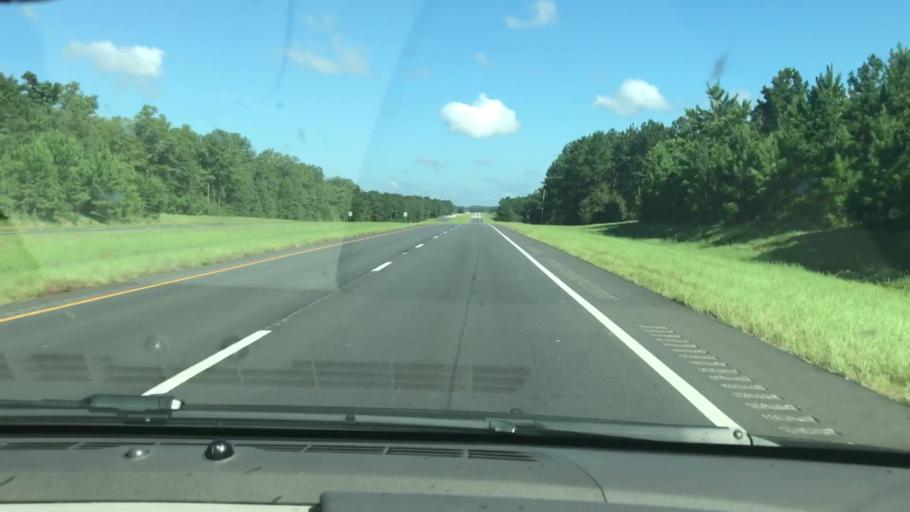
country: US
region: Alabama
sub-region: Barbour County
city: Eufaula
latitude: 32.0560
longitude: -85.1365
